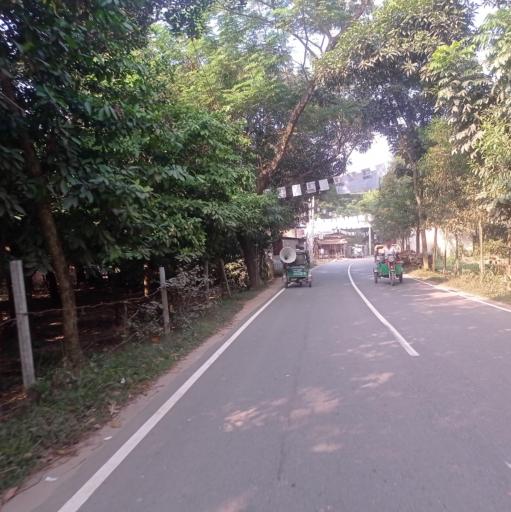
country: BD
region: Dhaka
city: Bhairab Bazar
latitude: 24.0386
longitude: 90.8321
